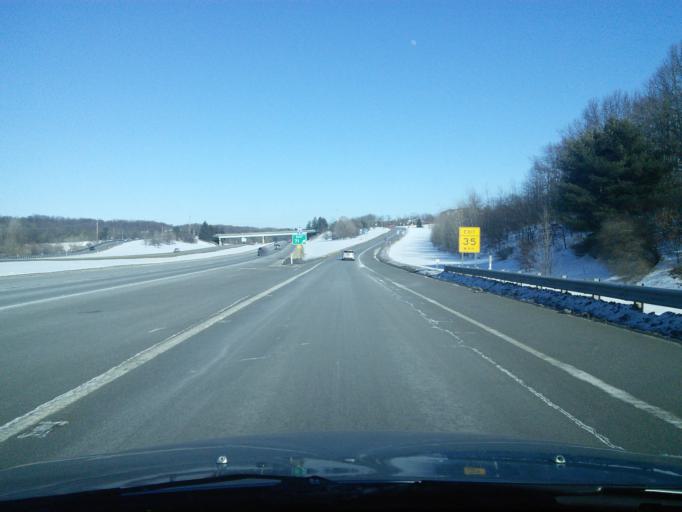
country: US
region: Pennsylvania
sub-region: Centre County
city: Park Forest Village
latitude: 40.8174
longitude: -77.9054
